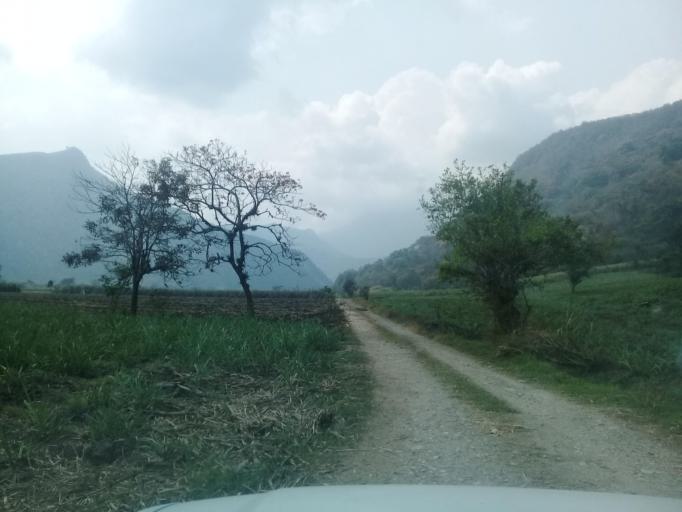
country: MX
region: Veracruz
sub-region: Ixtaczoquitlan
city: Capoluca
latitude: 18.8181
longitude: -96.9950
